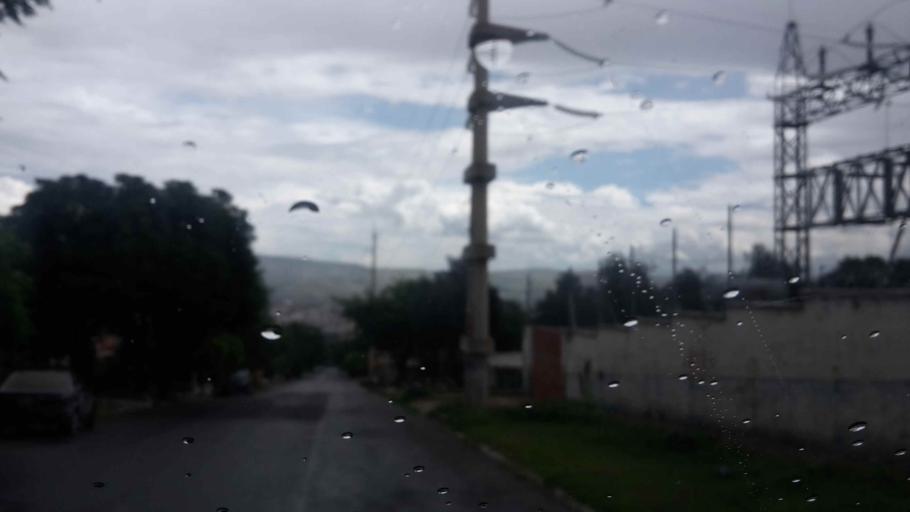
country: BO
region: Cochabamba
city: Cochabamba
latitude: -17.3616
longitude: -66.1593
